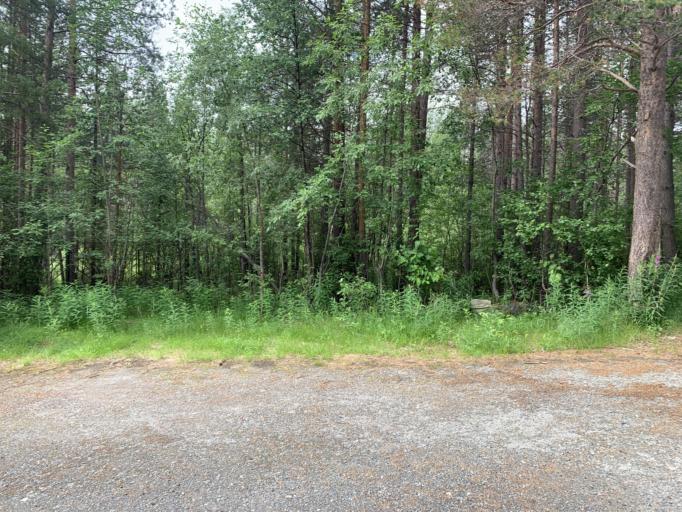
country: RU
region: Murmansk
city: Afrikanda
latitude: 67.6528
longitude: 32.8906
